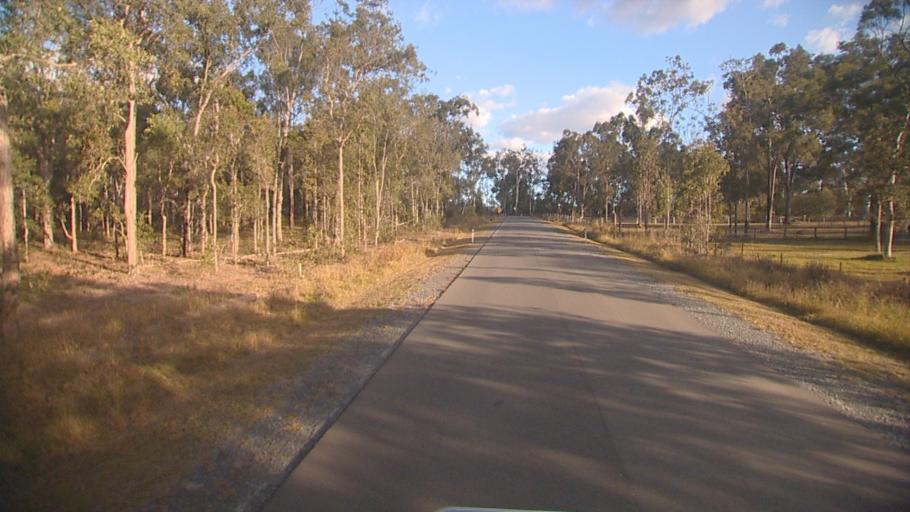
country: AU
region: Queensland
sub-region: Logan
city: Cedar Vale
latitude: -27.8572
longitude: 153.0925
